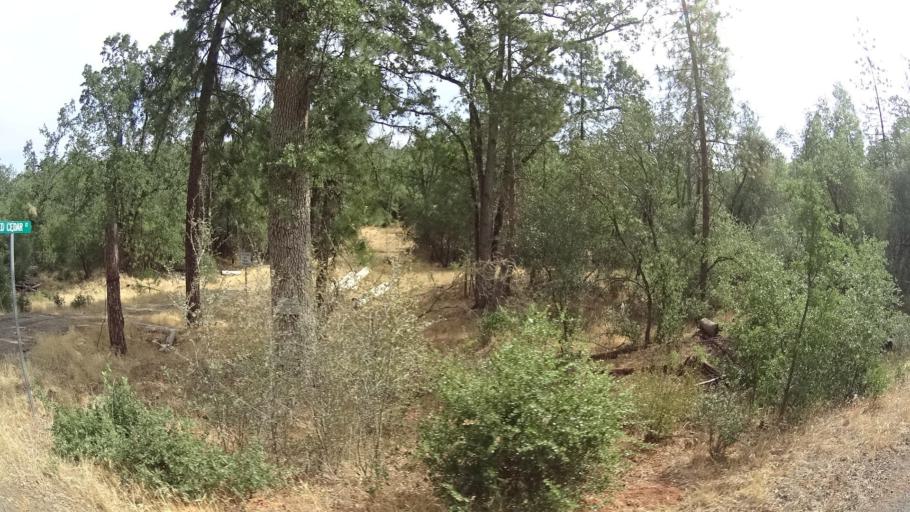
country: US
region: California
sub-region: Mariposa County
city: Mariposa
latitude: 37.5373
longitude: -119.9859
